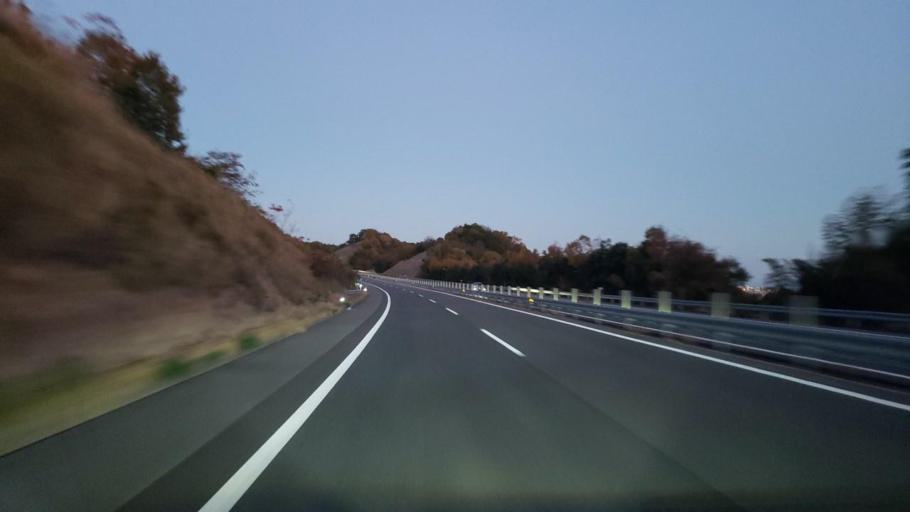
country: JP
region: Tokushima
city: Narutocho-mitsuishi
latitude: 34.1591
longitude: 134.5243
